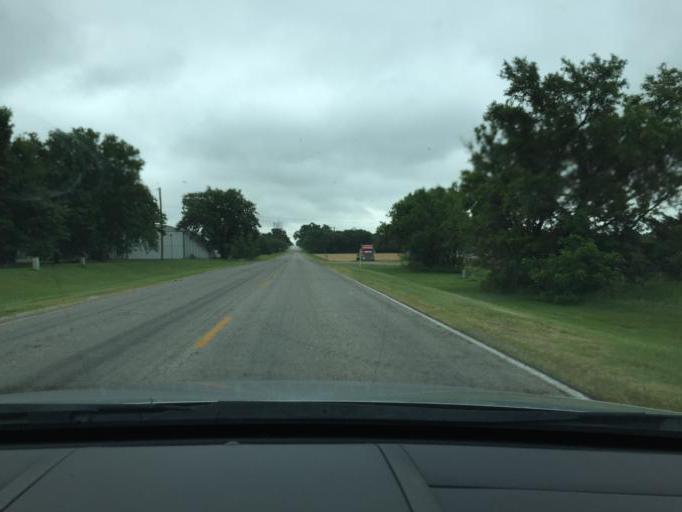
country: US
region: Kansas
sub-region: McPherson County
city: Moundridge
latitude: 38.2030
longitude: -97.5355
